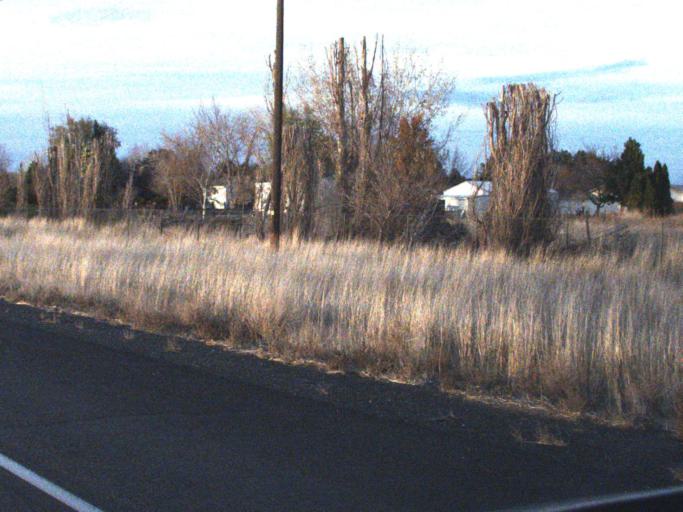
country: US
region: Washington
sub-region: Walla Walla County
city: Burbank
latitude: 46.1920
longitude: -118.9880
